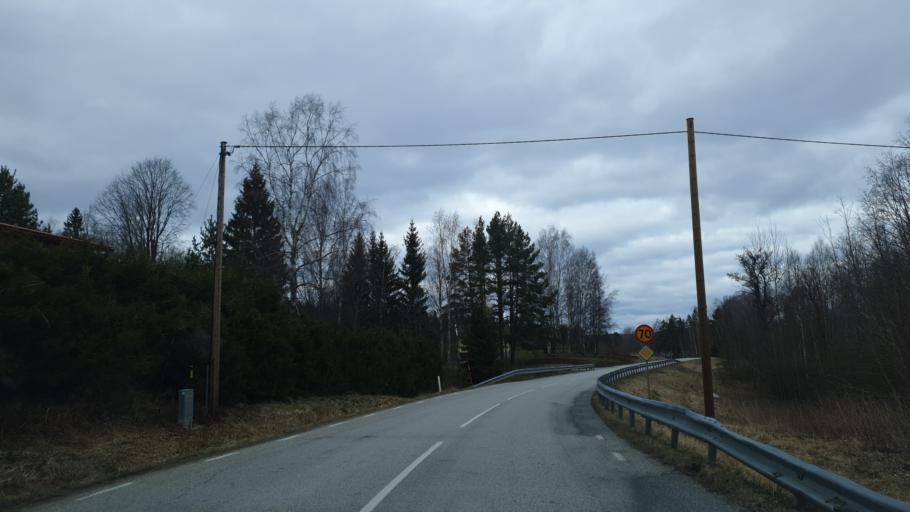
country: SE
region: OErebro
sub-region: Nora Kommun
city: As
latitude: 59.6053
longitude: 14.9291
